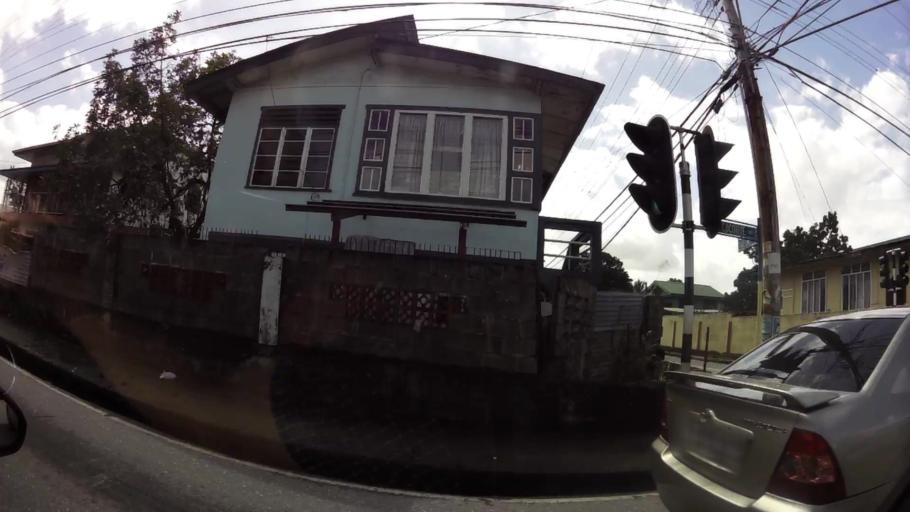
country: TT
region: Borough of Arima
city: Arima
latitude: 10.6380
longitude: -61.2772
